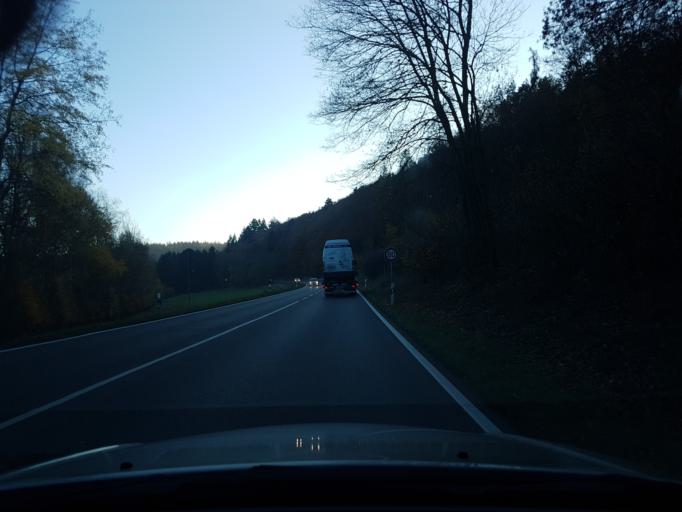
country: DE
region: Hesse
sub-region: Regierungsbezirk Darmstadt
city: Idstein
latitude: 50.1961
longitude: 8.2439
